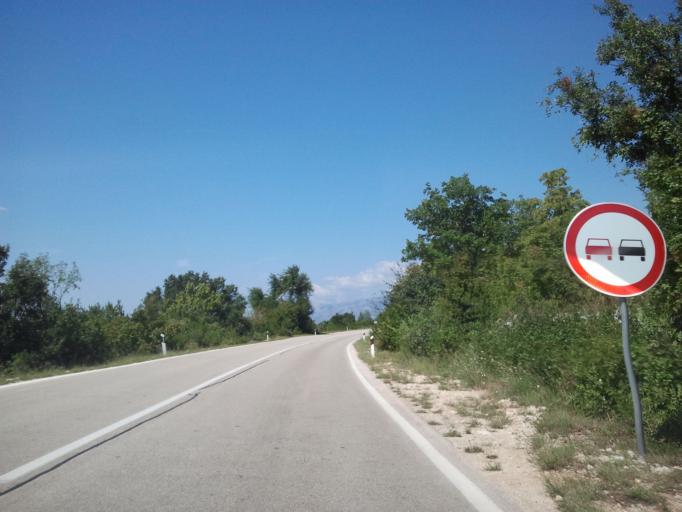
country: HR
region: Zadarska
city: Krusevo
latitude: 44.1742
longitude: 15.6186
